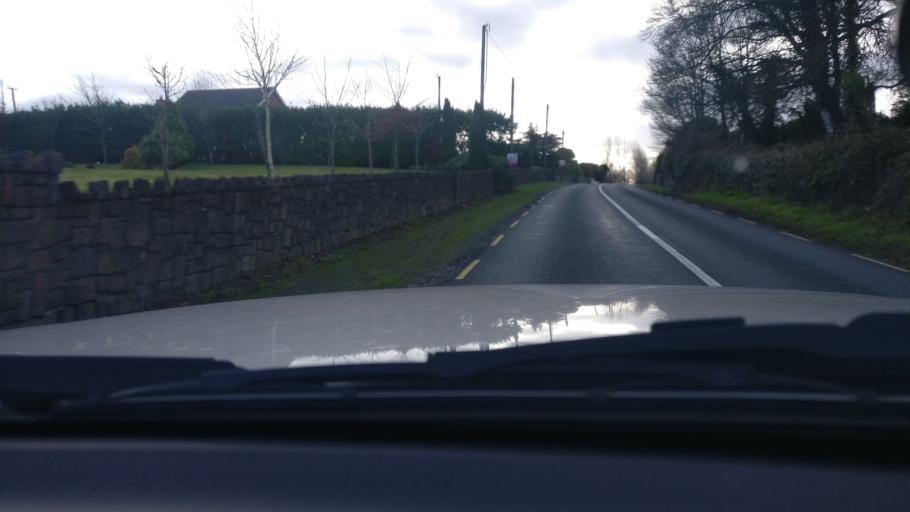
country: IE
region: Connaught
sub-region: County Galway
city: Ballinasloe
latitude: 53.3048
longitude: -8.2444
